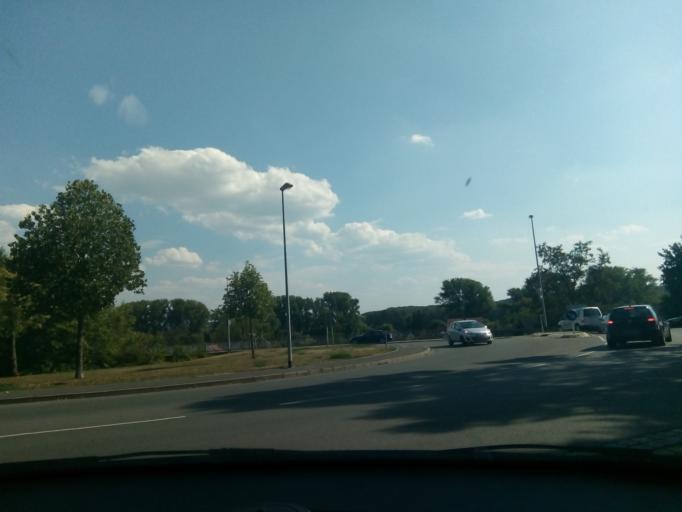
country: DE
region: Bavaria
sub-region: Regierungsbezirk Unterfranken
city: Hassfurt
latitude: 50.0326
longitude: 10.4973
